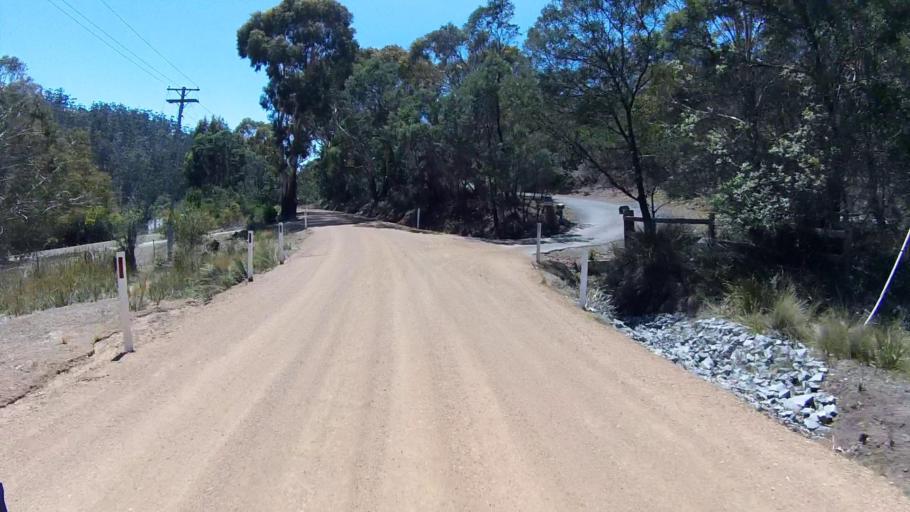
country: AU
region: Tasmania
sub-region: Clarence
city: Cambridge
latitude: -42.8514
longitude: 147.4371
